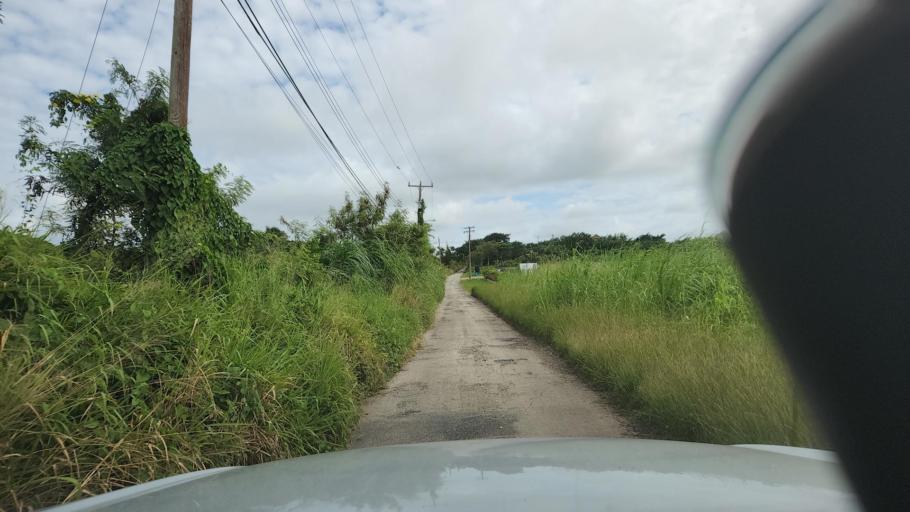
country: BB
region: Saint Lucy
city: Checker Hall
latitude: 13.2971
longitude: -59.6079
